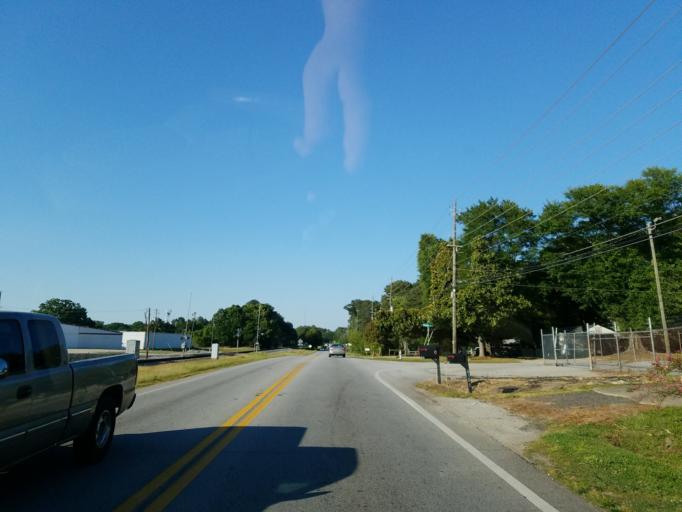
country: US
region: Georgia
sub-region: Douglas County
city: Douglasville
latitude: 33.7677
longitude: -84.7161
